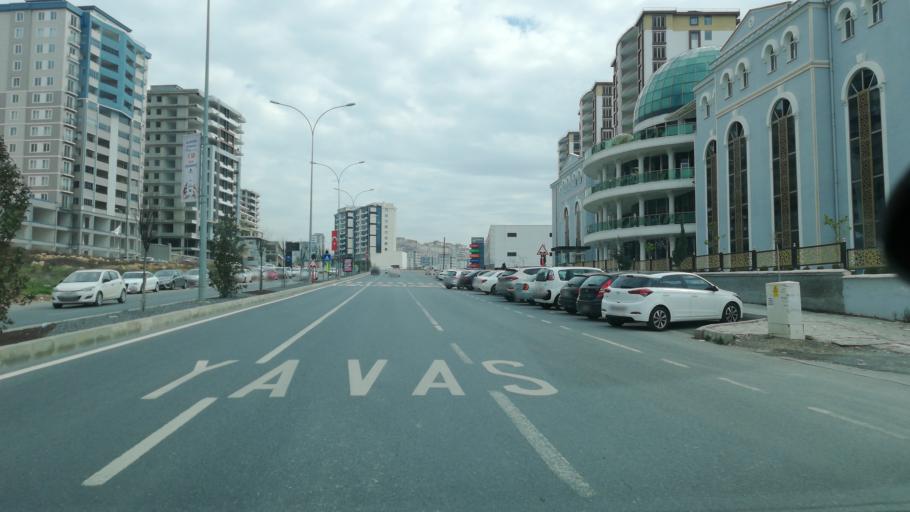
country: TR
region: Kahramanmaras
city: Kahramanmaras
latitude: 37.5857
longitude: 36.8490
